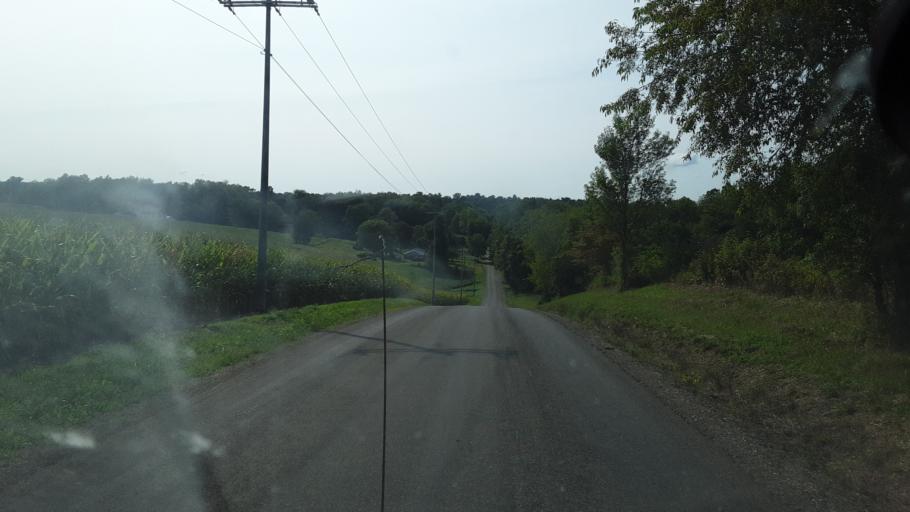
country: US
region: Ohio
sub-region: Knox County
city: Danville
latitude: 40.4227
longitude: -82.2827
